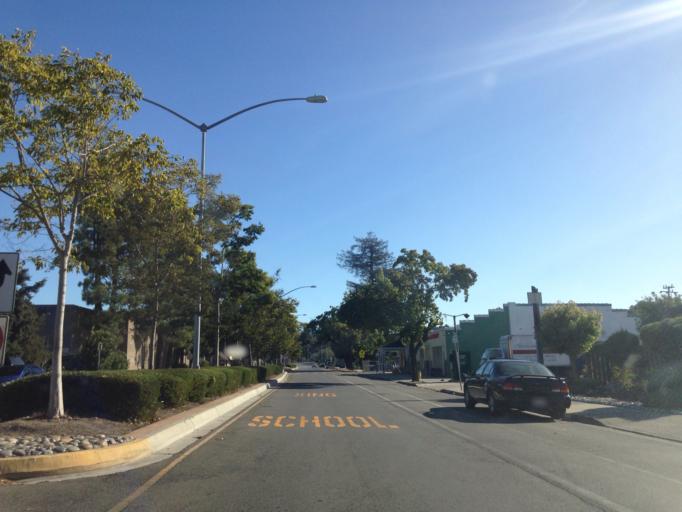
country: US
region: California
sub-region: Contra Costa County
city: Rodeo
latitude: 38.0306
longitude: -122.2665
